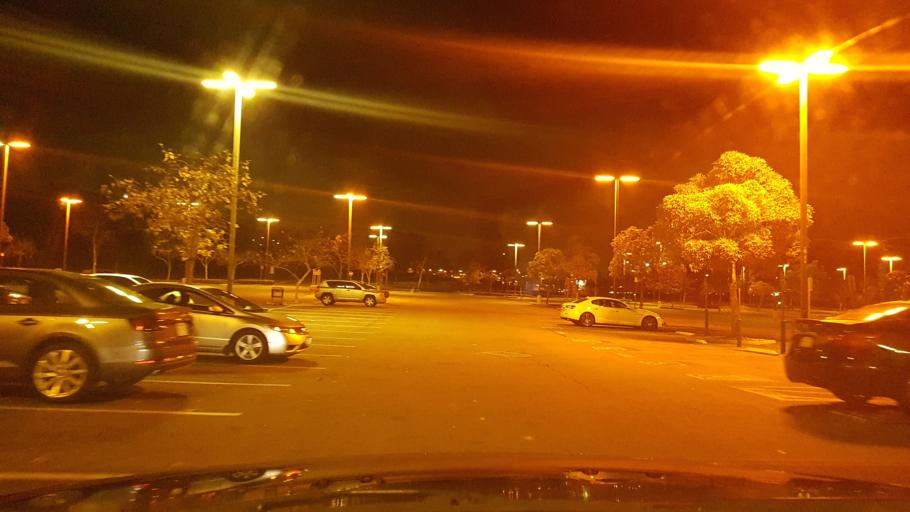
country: US
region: California
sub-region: San Diego County
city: San Diego
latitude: 32.8022
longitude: -117.1148
